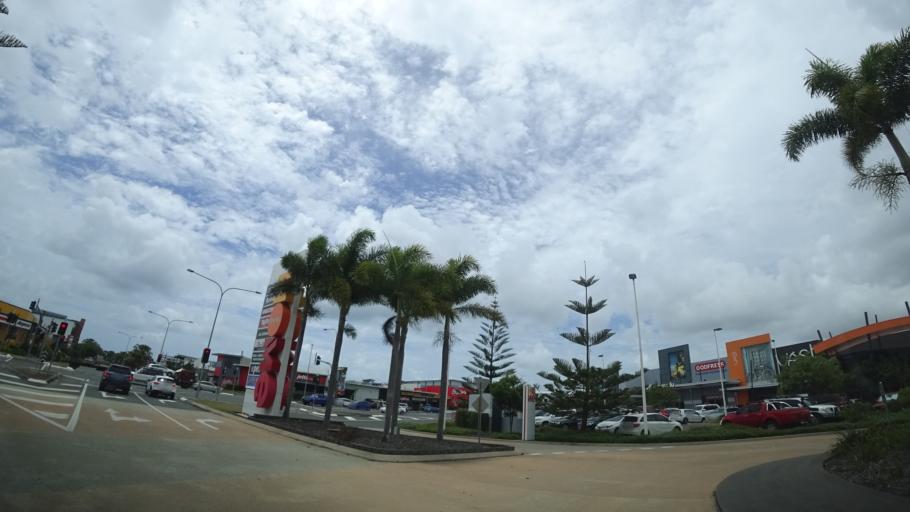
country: AU
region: Queensland
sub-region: Sunshine Coast
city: Dicky Beach
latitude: -26.7359
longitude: 153.1198
